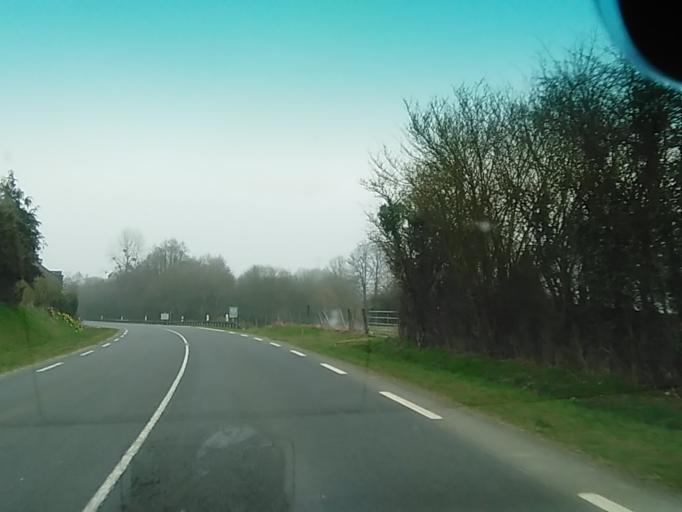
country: FR
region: Lower Normandy
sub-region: Departement de l'Orne
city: La Ferte-Mace
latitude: 48.6056
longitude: -0.3275
